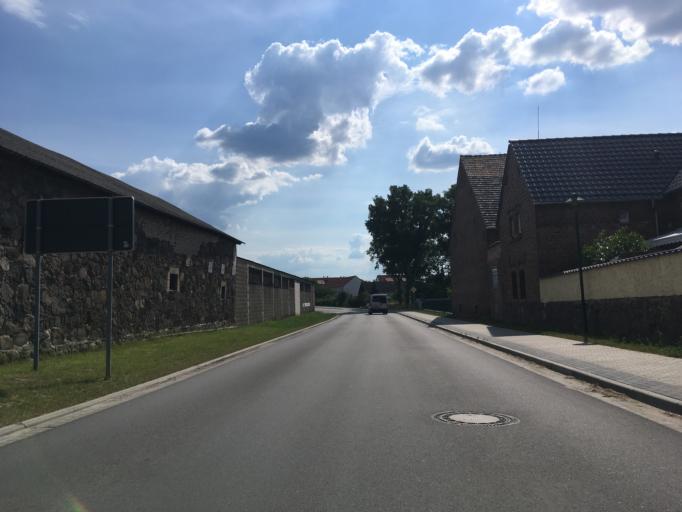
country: DE
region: Brandenburg
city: Steinhofel
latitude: 52.4239
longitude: 14.1111
